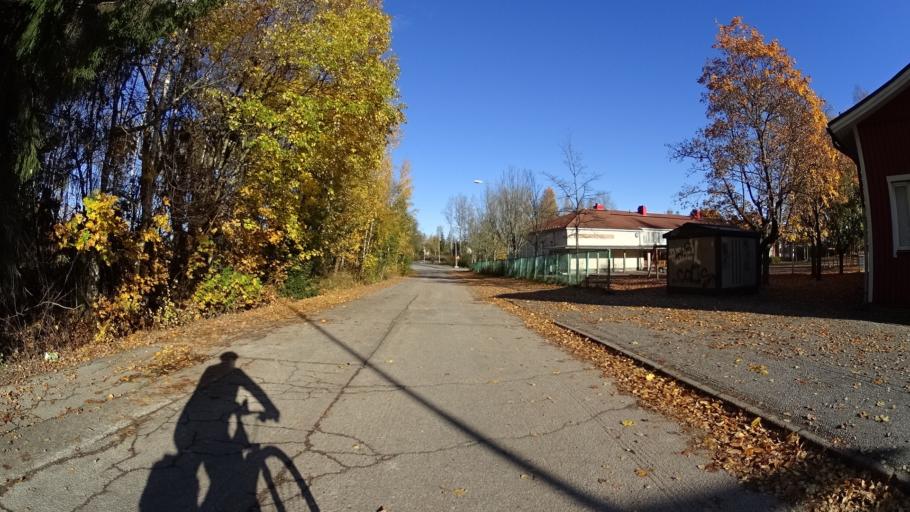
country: FI
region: Uusimaa
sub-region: Helsinki
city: Kilo
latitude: 60.2937
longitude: 24.8515
